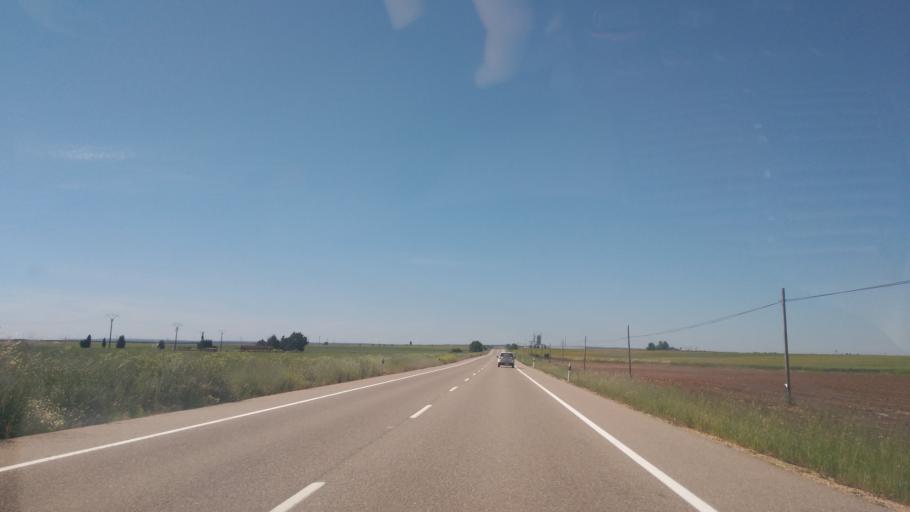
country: ES
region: Castille and Leon
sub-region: Provincia de Salamanca
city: Calzada de Valdunciel
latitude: 41.0734
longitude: -5.6911
